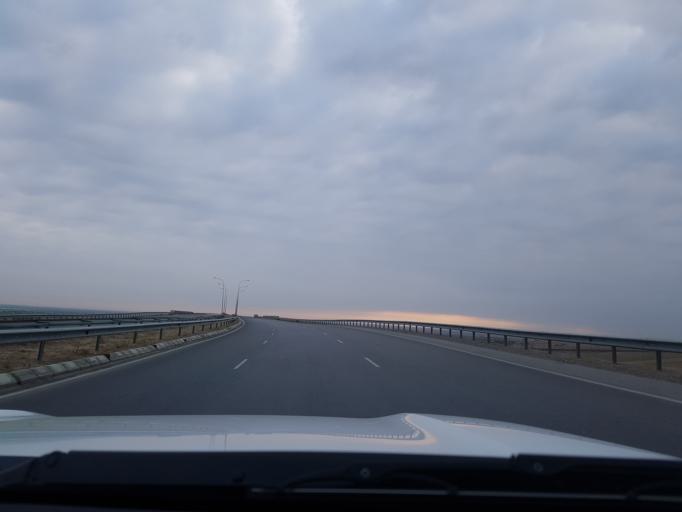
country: IR
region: Razavi Khorasan
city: Dargaz
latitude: 37.6817
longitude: 59.0762
